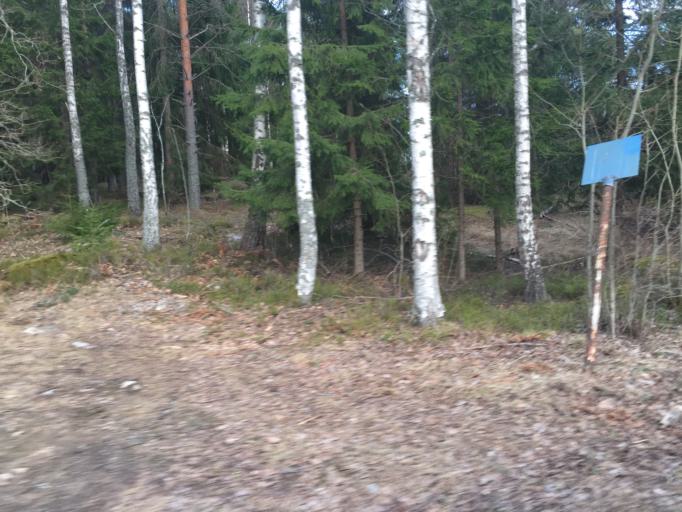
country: SE
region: Soedermanland
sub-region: Vingakers Kommun
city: Vingaker
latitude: 58.9918
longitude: 15.6862
